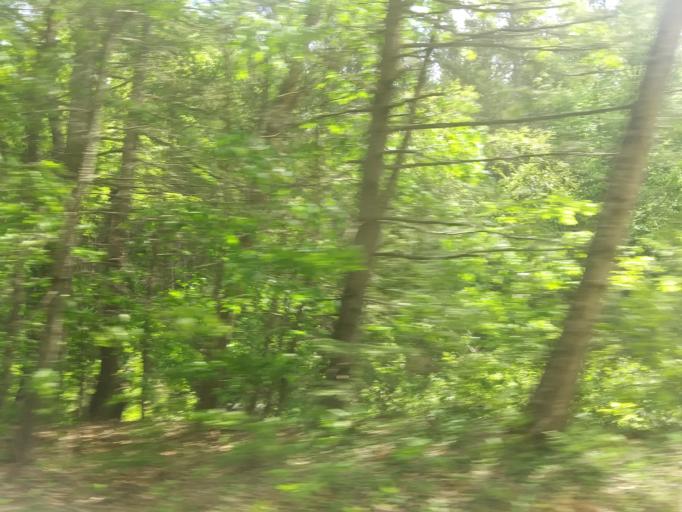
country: US
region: Massachusetts
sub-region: Franklin County
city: Buckland
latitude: 42.5808
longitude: -72.8212
